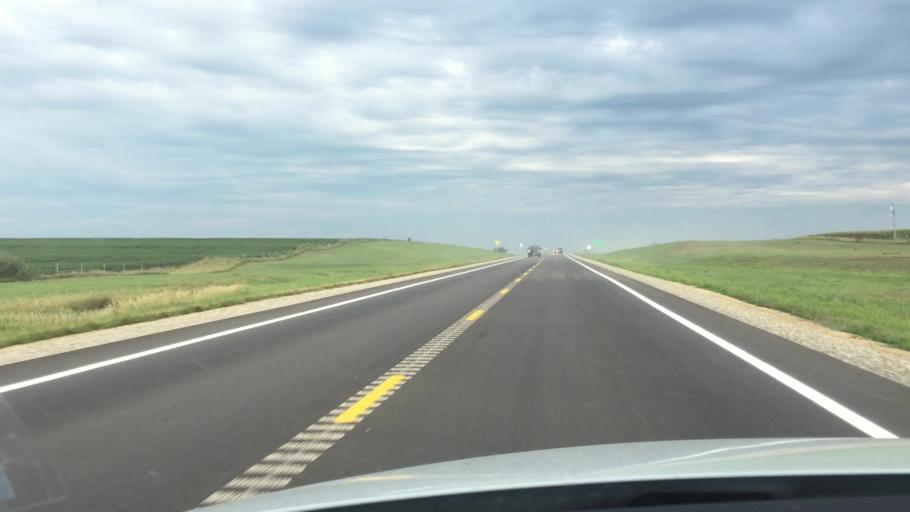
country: US
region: Kansas
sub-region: Brown County
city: Hiawatha
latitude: 39.8412
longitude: -95.4034
